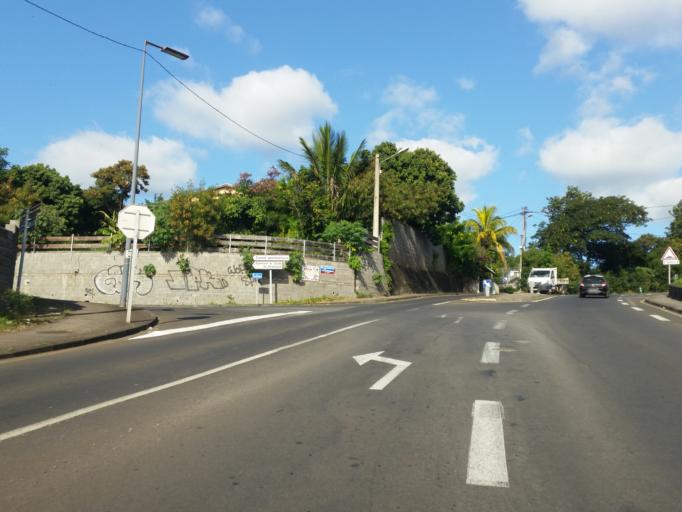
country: RE
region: Reunion
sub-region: Reunion
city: Sainte-Marie
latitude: -20.9101
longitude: 55.5018
